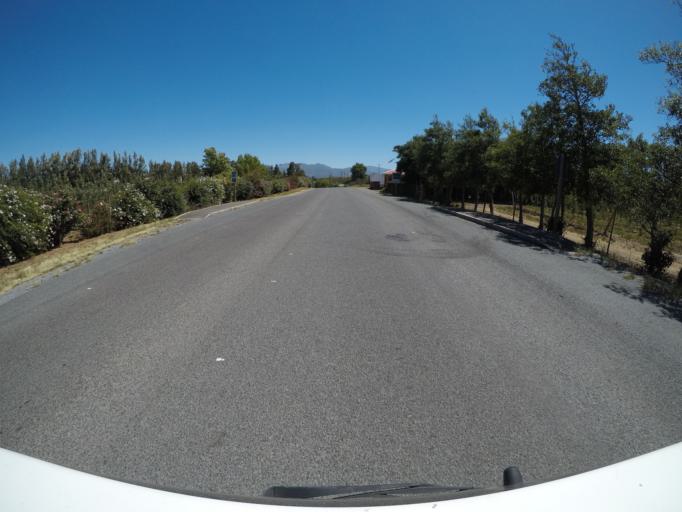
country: ZA
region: Western Cape
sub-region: Overberg District Municipality
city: Grabouw
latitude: -34.1894
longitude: 19.0400
